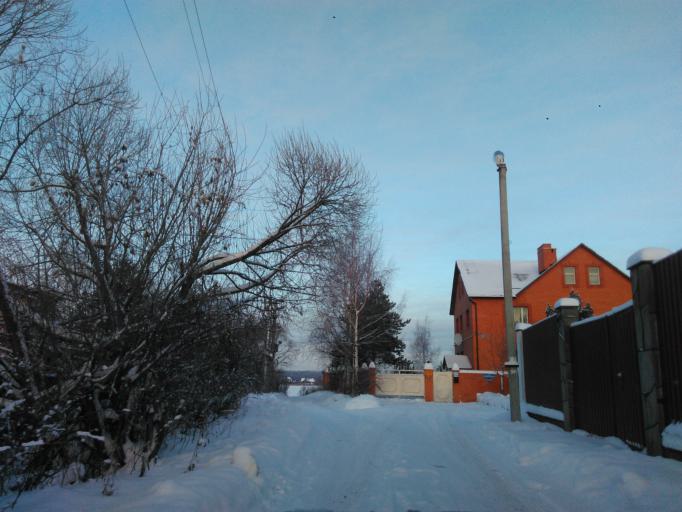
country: RU
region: Tverskaya
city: Zavidovo
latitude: 56.6366
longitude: 36.6181
